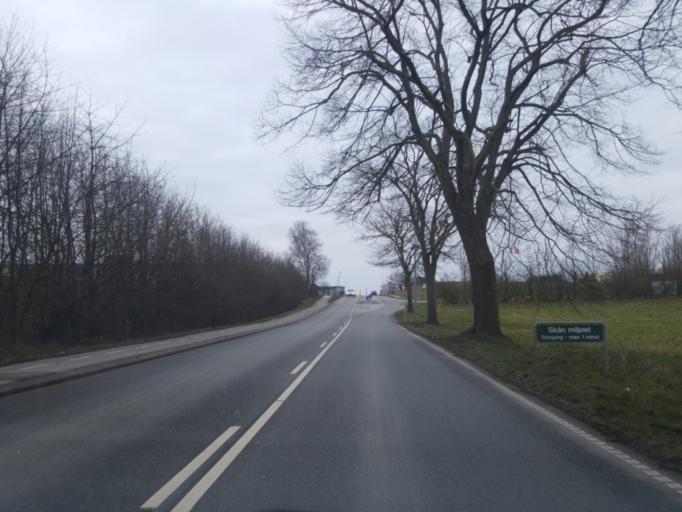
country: DK
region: Zealand
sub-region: Vordingborg Kommune
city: Vordingborg
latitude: 55.0153
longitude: 11.9223
